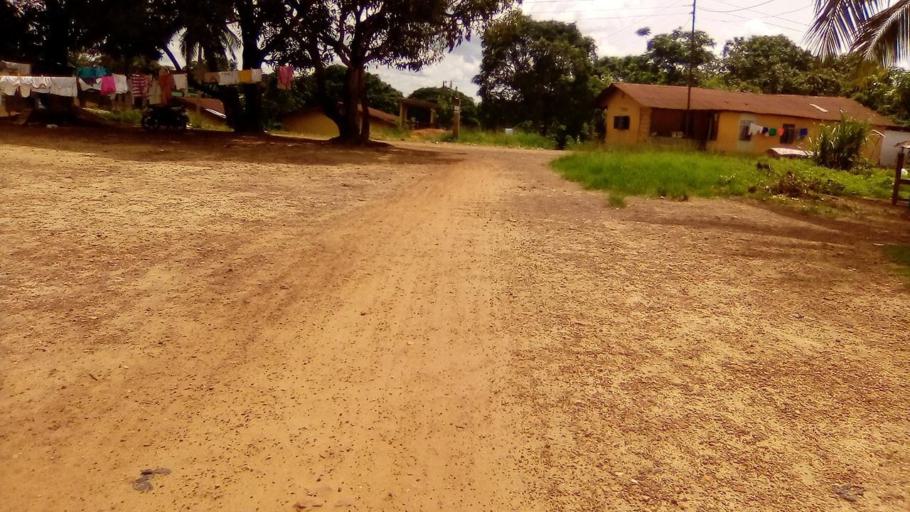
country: SL
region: Southern Province
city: Bo
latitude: 7.9636
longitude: -11.7221
